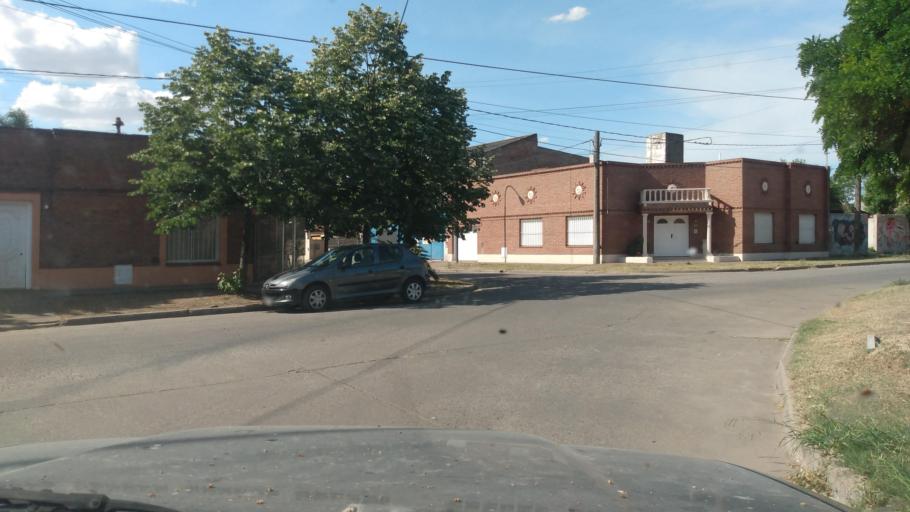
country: AR
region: Buenos Aires
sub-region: Partido de Lujan
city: Lujan
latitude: -34.5564
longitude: -59.1081
